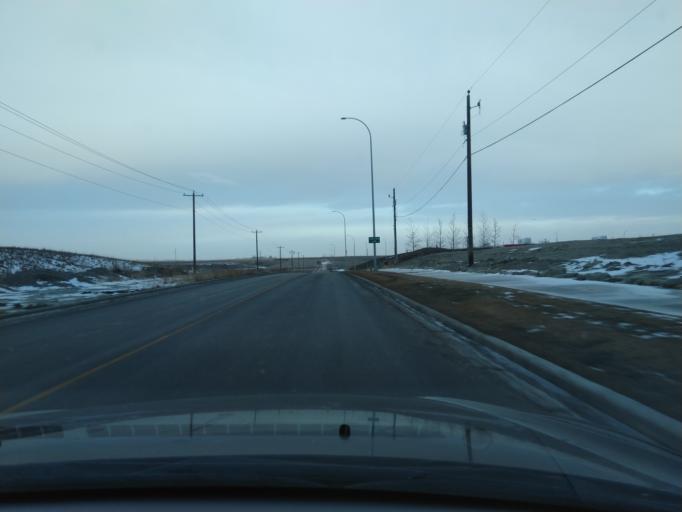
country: CA
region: Alberta
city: Calgary
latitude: 51.1630
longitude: -114.0248
